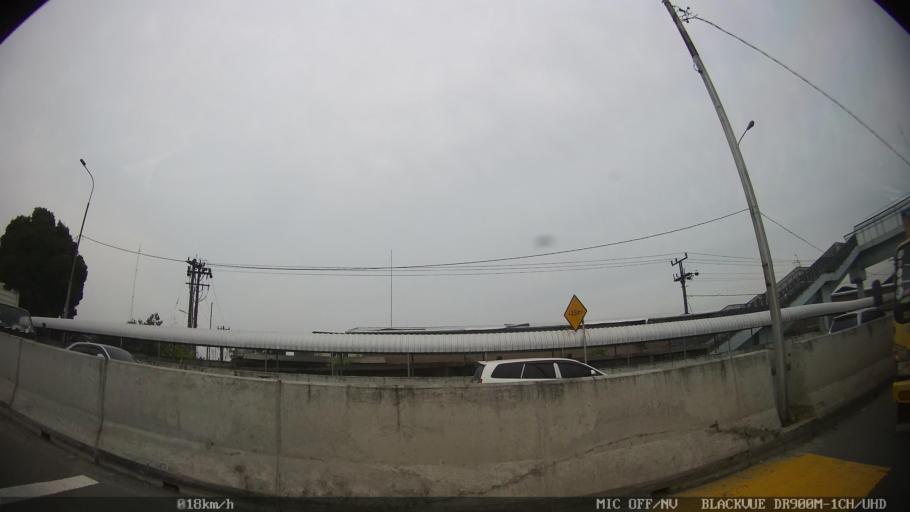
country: ID
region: North Sumatra
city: Deli Tua
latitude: 3.5382
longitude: 98.7221
